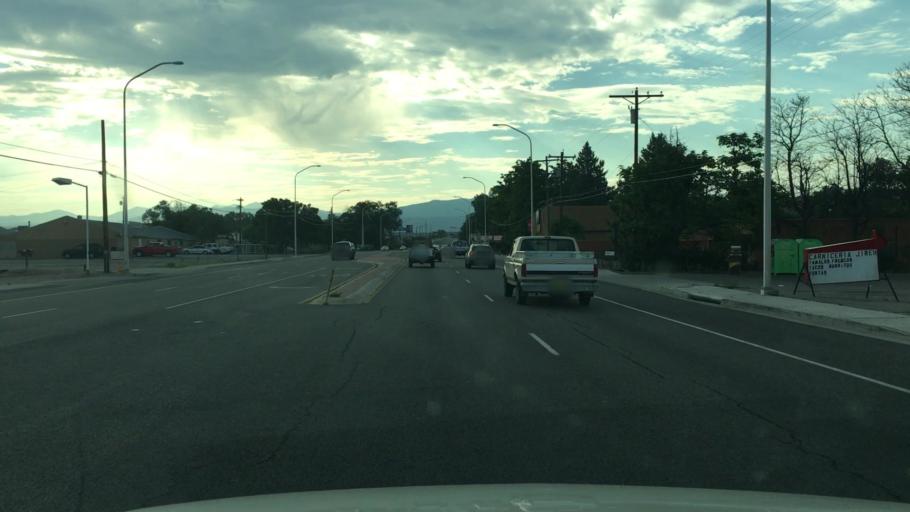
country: US
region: New Mexico
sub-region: Rio Arriba County
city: Espanola
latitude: 35.9880
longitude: -106.0634
